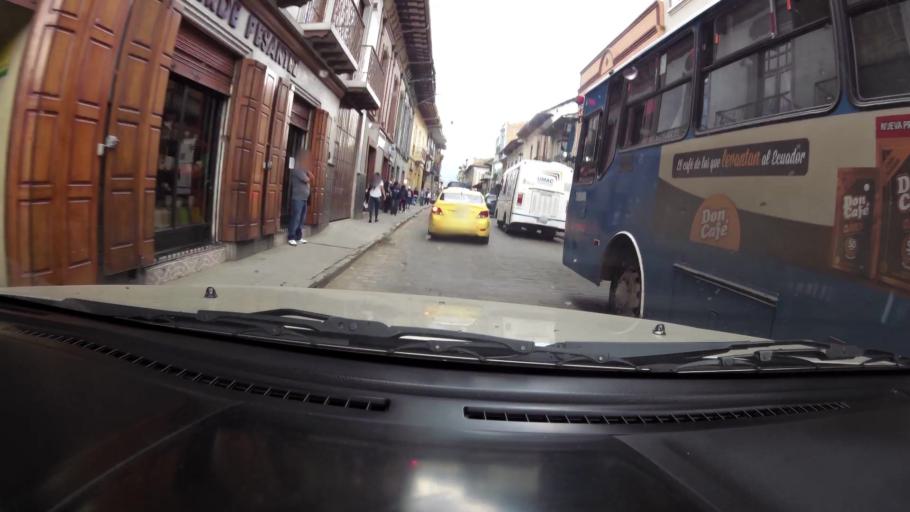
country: EC
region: Azuay
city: Cuenca
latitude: -2.8983
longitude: -79.0073
